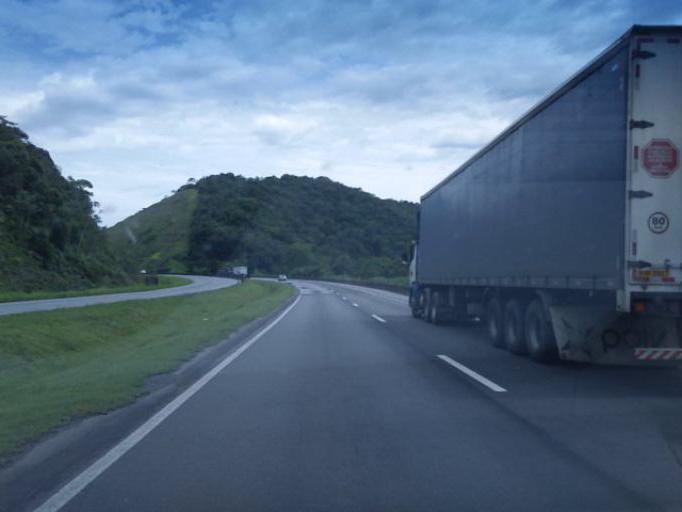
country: BR
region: Sao Paulo
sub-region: Miracatu
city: Miracatu
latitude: -24.2244
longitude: -47.3648
